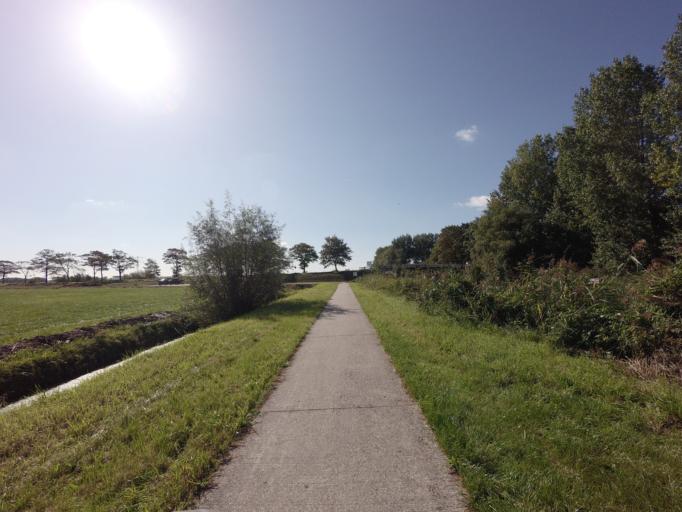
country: NL
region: Friesland
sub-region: Gemeente Boarnsterhim
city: Reduzum
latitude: 53.1496
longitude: 5.7638
